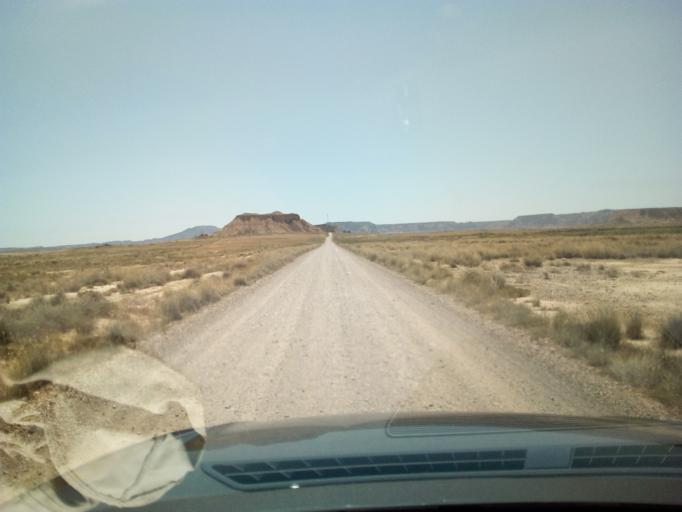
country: ES
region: Navarre
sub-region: Provincia de Navarra
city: Arguedas
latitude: 42.1994
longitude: -1.4956
